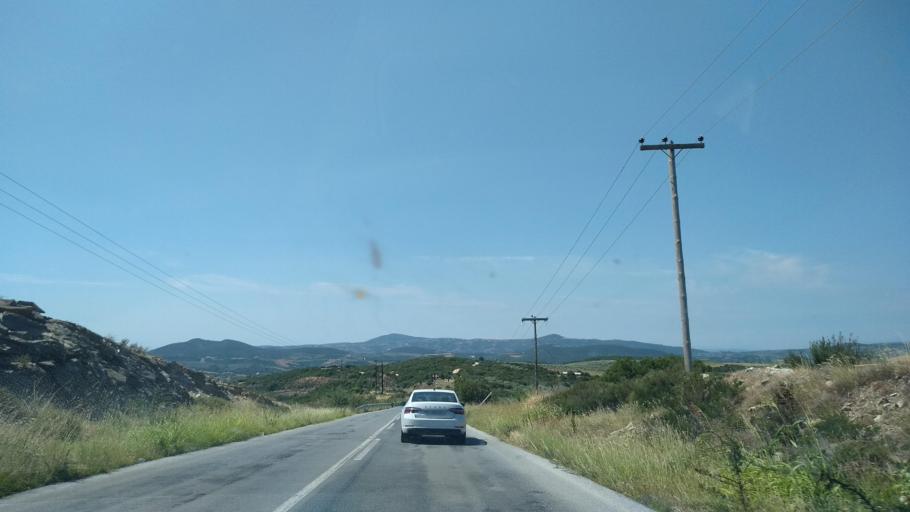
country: GR
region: Central Macedonia
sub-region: Nomos Chalkidikis
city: Megali Panagia
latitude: 40.4139
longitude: 23.6941
